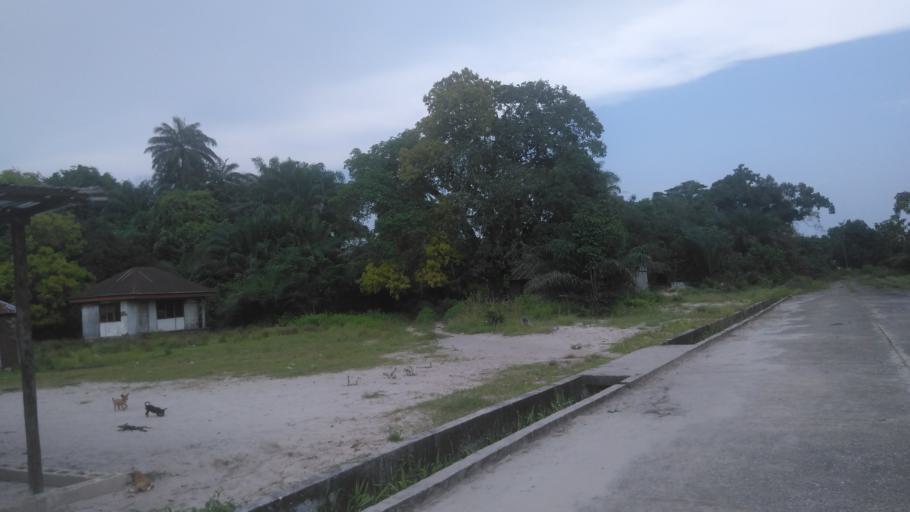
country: NG
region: Delta
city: Sapele
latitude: 5.8405
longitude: 5.1253
